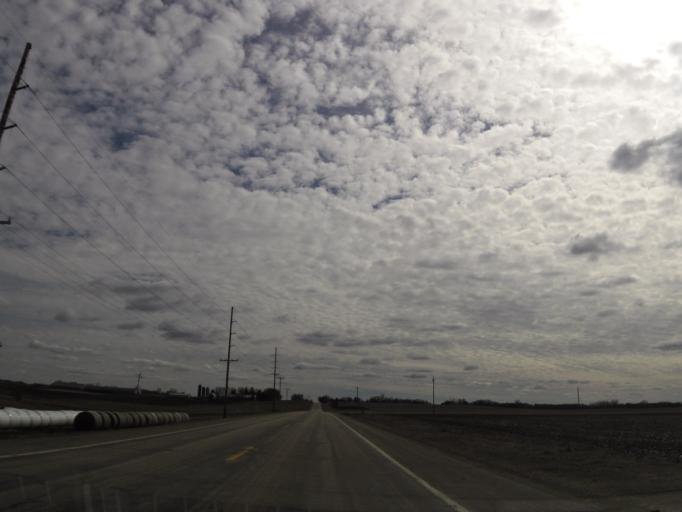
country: US
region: Minnesota
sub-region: Olmsted County
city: Rochester
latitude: 43.9364
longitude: -92.4086
